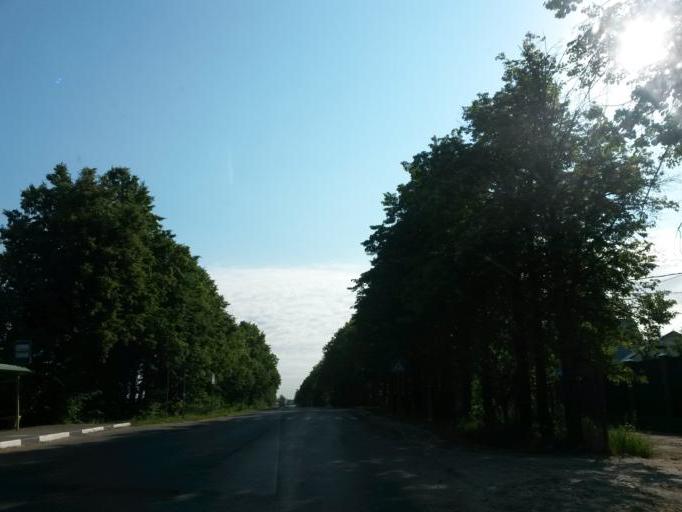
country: RU
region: Moscow
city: Zyablikovo
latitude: 55.5995
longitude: 37.7898
